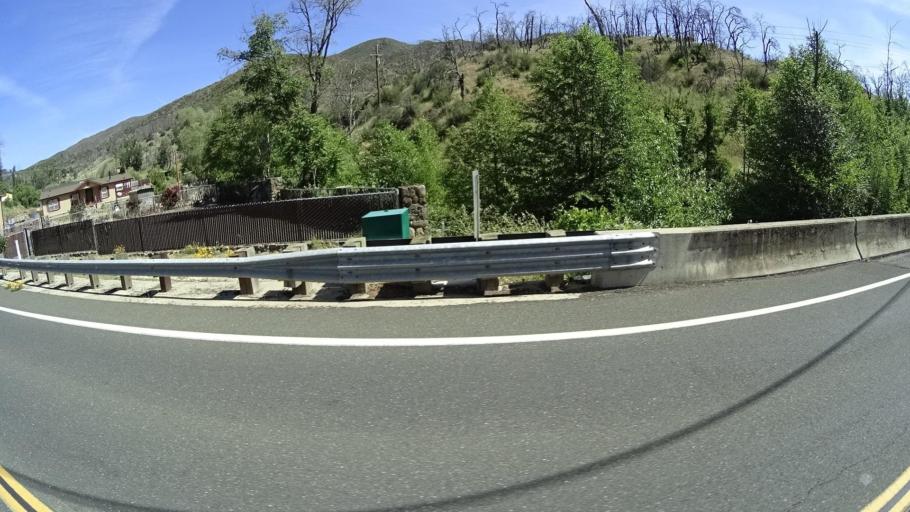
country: US
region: California
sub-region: Lake County
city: Cobb
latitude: 38.7784
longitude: -122.6812
